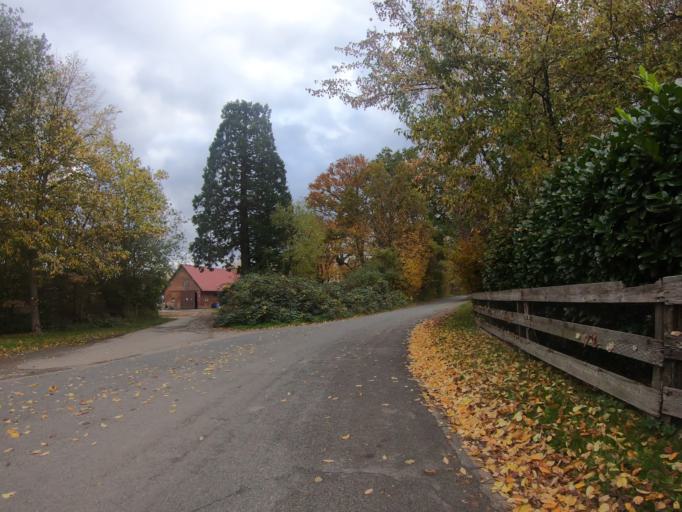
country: DE
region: Lower Saxony
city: Adenbuettel
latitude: 52.4027
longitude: 10.4739
